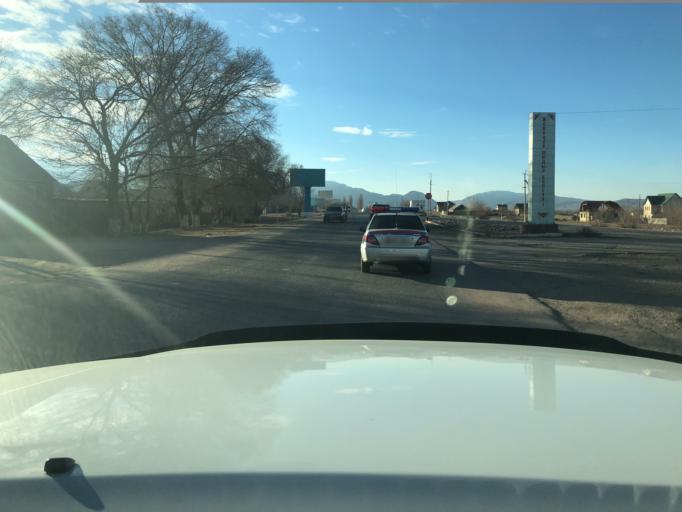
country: KG
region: Ysyk-Koel
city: Bokombayevskoye
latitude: 42.1155
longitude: 76.9815
